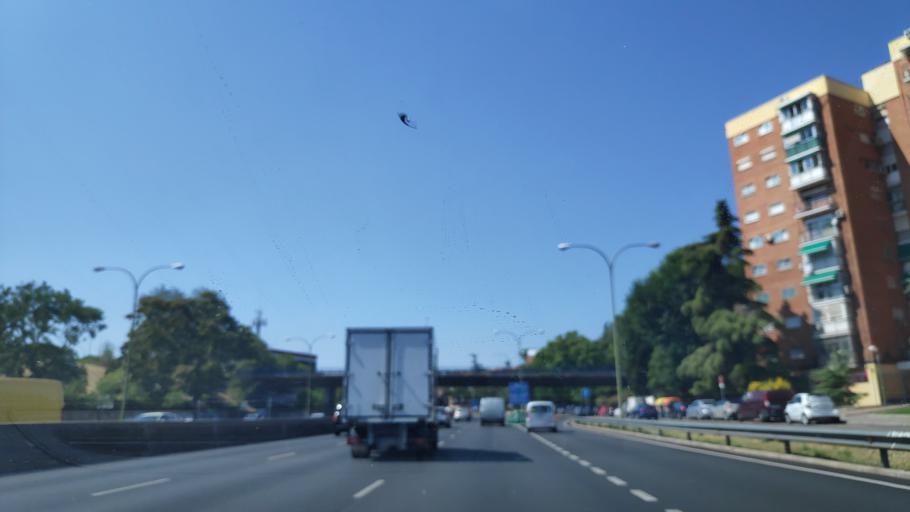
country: ES
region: Madrid
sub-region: Provincia de Madrid
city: Usera
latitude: 40.3908
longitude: -3.7109
